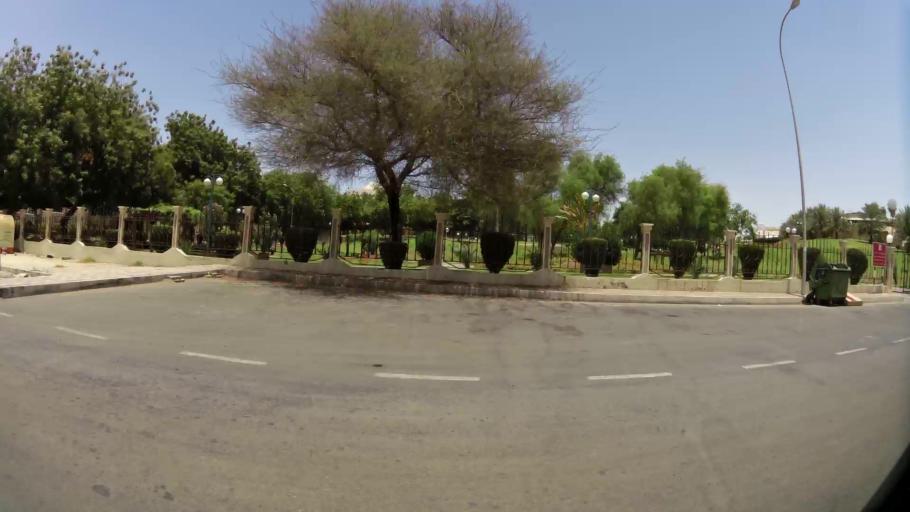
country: OM
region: Muhafazat Masqat
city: Bawshar
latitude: 23.6121
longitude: 58.4778
